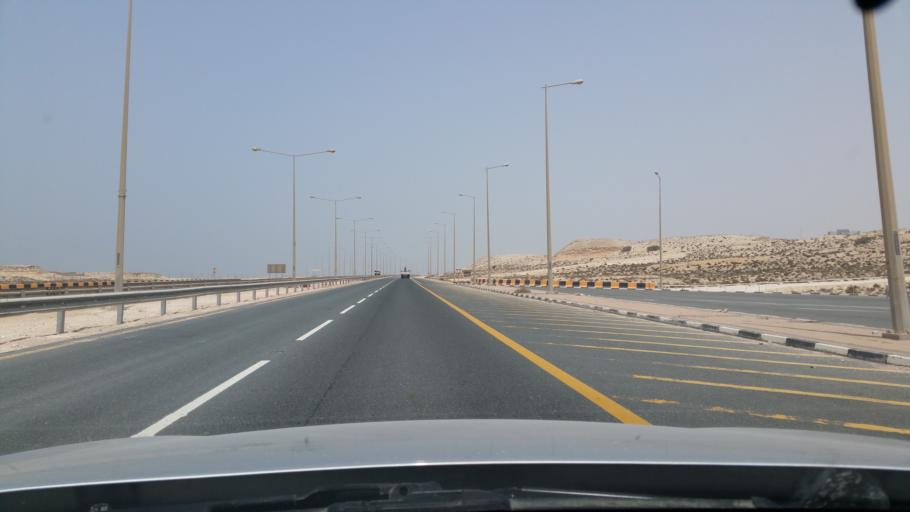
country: QA
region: Baladiyat ar Rayyan
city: Dukhan
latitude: 25.3495
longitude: 50.7818
